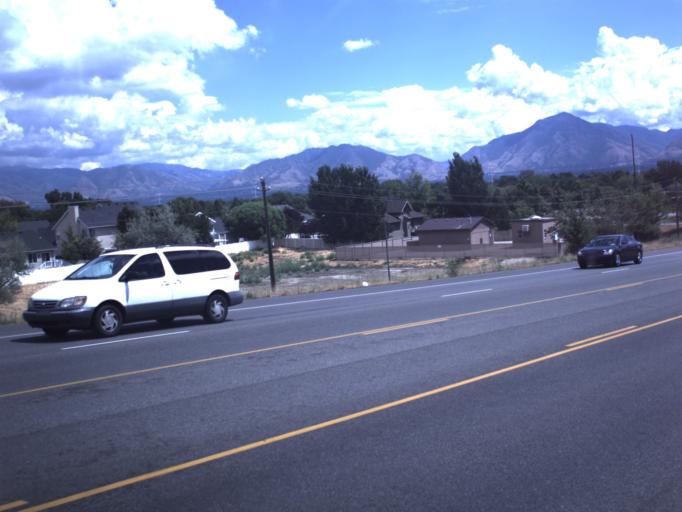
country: US
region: Utah
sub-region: Salt Lake County
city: Taylorsville
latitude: 40.6530
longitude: -111.9277
